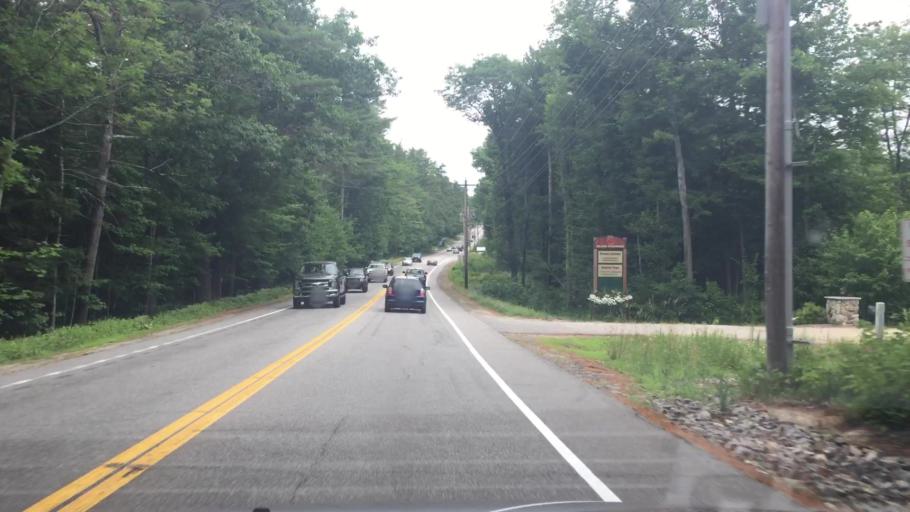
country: US
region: New Hampshire
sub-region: Carroll County
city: Moultonborough
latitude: 43.7461
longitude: -71.4052
